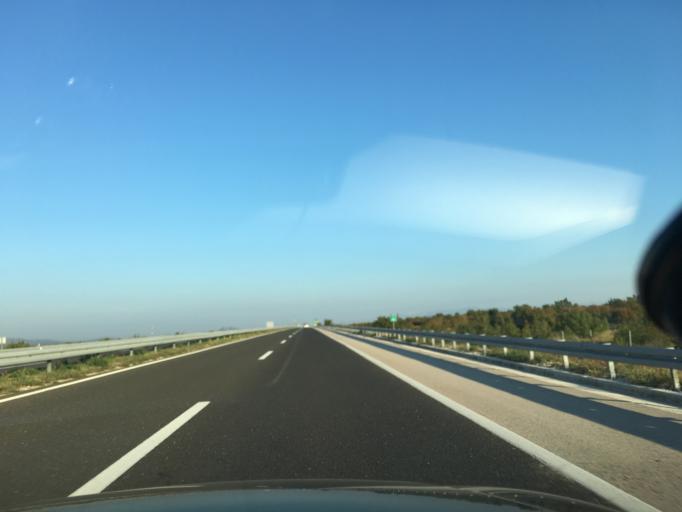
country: HR
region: Sibensko-Kniniska
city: Zaton
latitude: 43.8786
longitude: 15.8000
